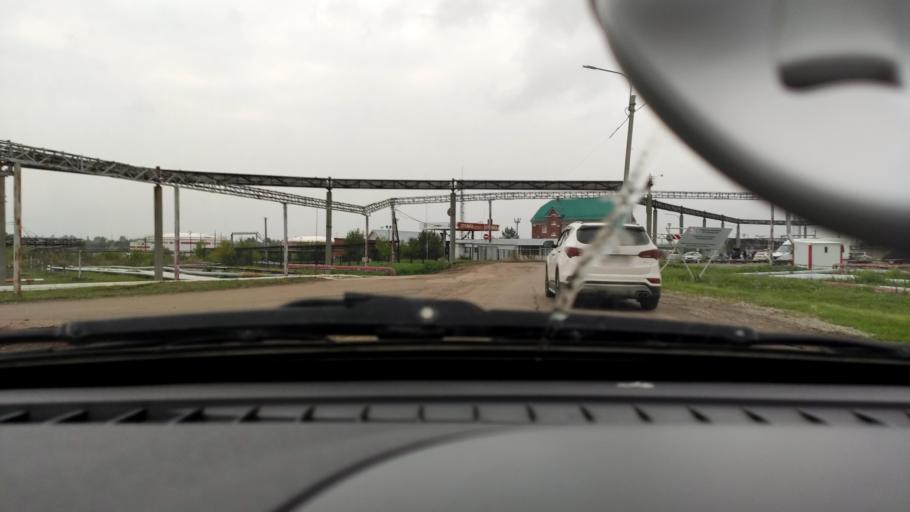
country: RU
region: Perm
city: Gamovo
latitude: 57.9086
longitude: 56.1493
